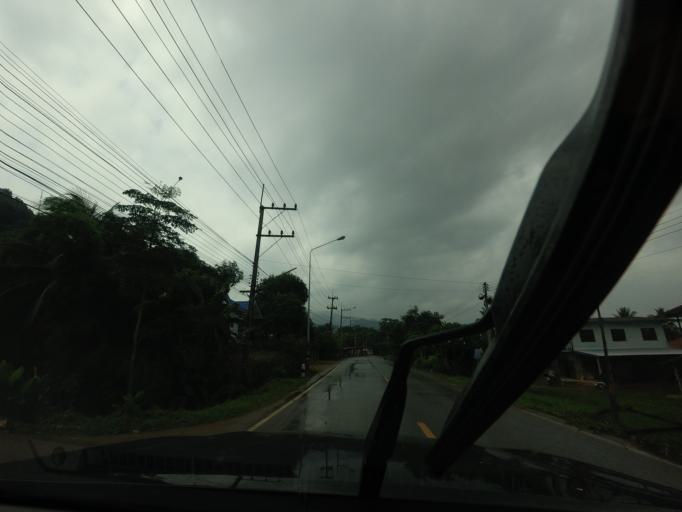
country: TH
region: Nong Khai
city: Sangkhom
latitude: 18.1063
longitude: 102.2297
